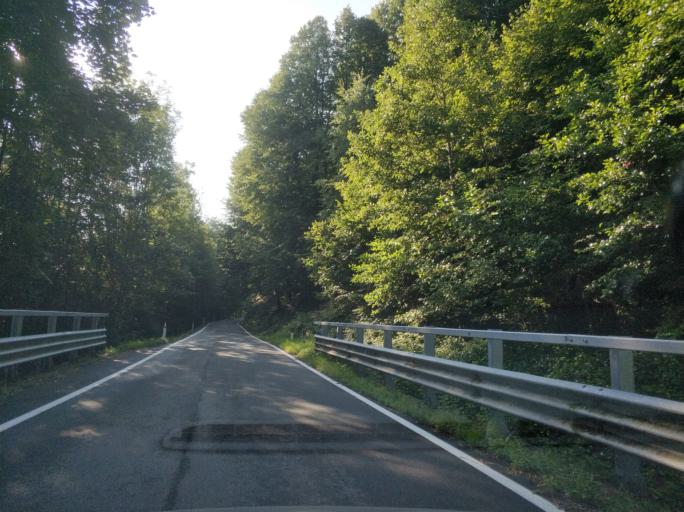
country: IT
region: Piedmont
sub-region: Provincia di Torino
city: Viu
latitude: 45.2276
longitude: 7.3757
